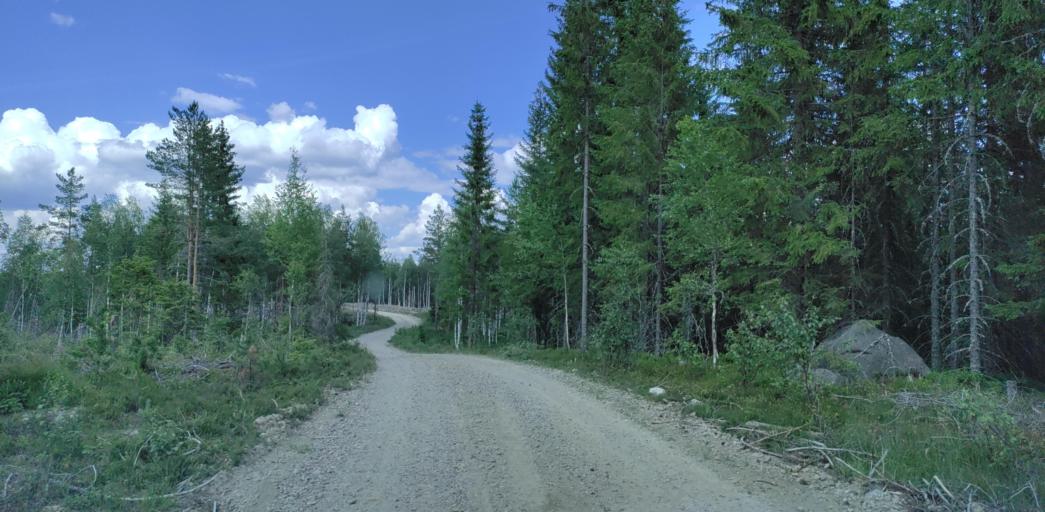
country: SE
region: Vaermland
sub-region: Hagfors Kommun
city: Ekshaerad
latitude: 60.0752
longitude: 13.3458
